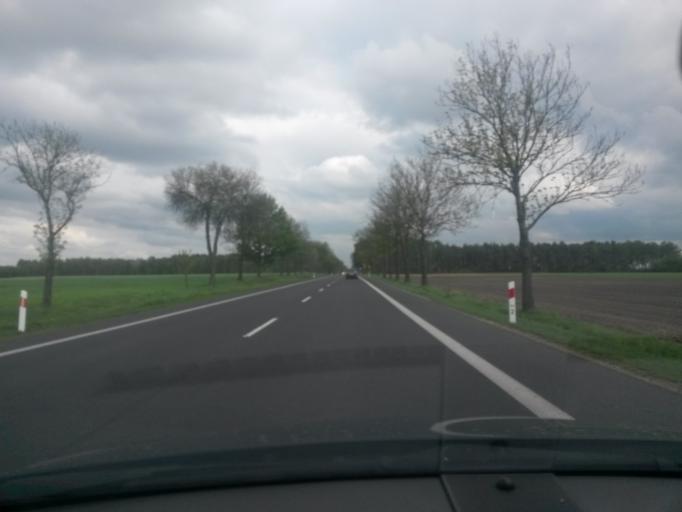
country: PL
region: Masovian Voivodeship
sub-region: Powiat sierpecki
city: Zawidz
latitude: 52.7844
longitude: 19.8945
